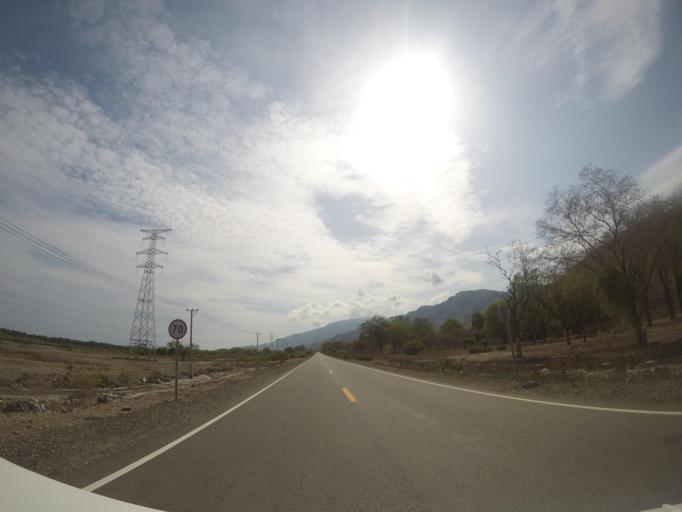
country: ID
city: Metinaro
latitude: -8.5112
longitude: 125.7878
